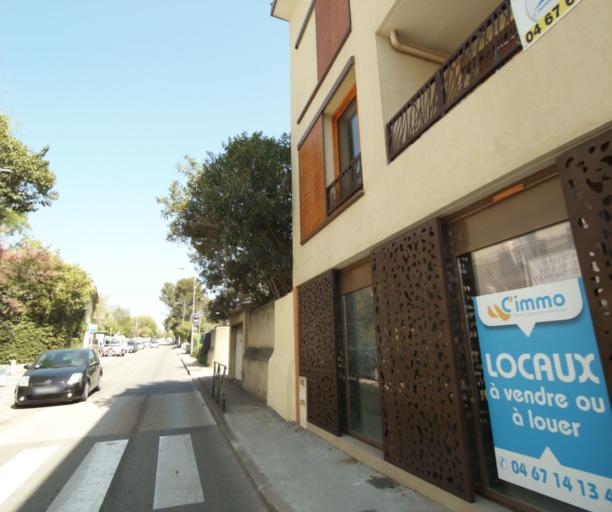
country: FR
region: Languedoc-Roussillon
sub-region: Departement de l'Herault
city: Castelnau-le-Lez
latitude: 43.6346
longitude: 3.8950
